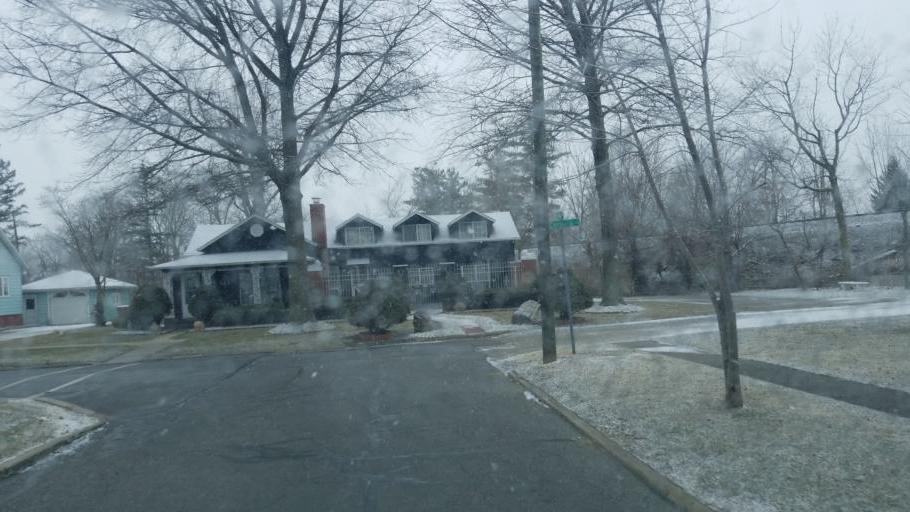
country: US
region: Ohio
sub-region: Defiance County
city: Hicksville
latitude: 41.2965
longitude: -84.7624
